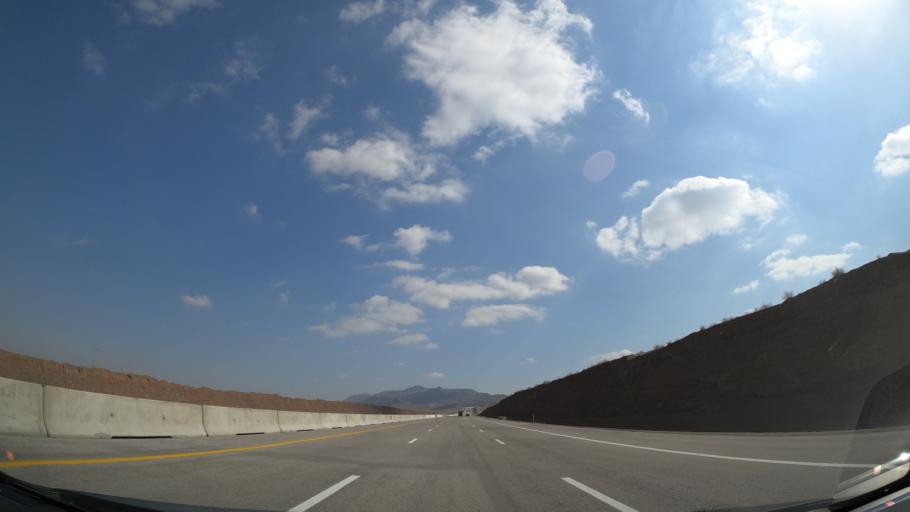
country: IR
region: Alborz
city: Eshtehard
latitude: 35.7048
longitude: 50.6128
